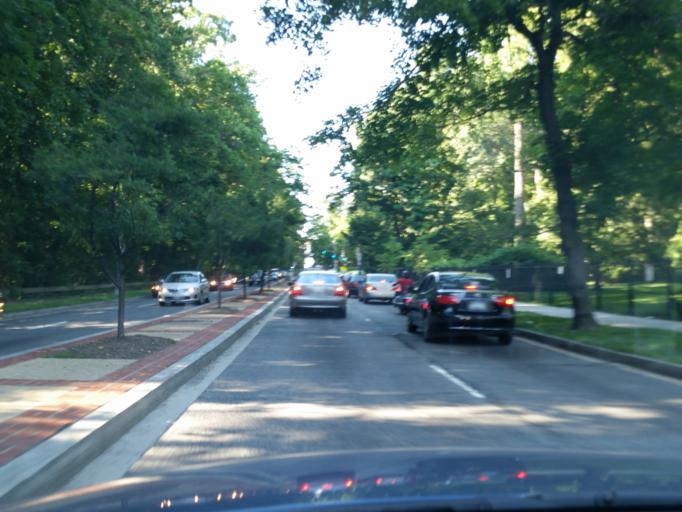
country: US
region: Maryland
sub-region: Montgomery County
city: Silver Spring
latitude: 38.9737
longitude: -77.0363
